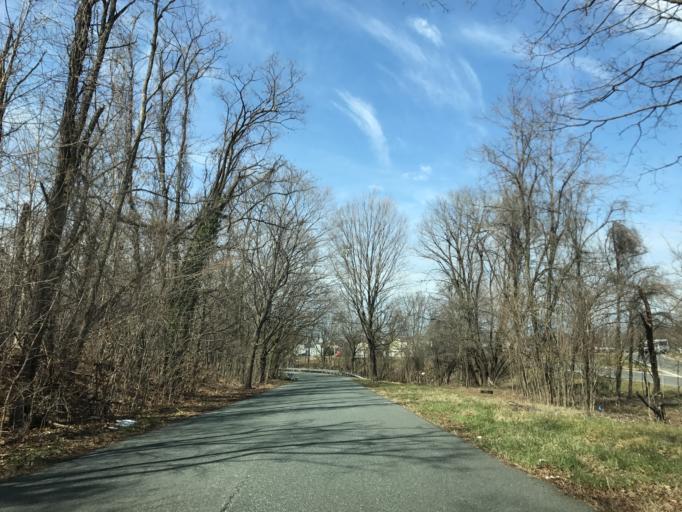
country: US
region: Maryland
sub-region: Baltimore County
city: Lansdowne
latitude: 39.2434
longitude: -76.6736
